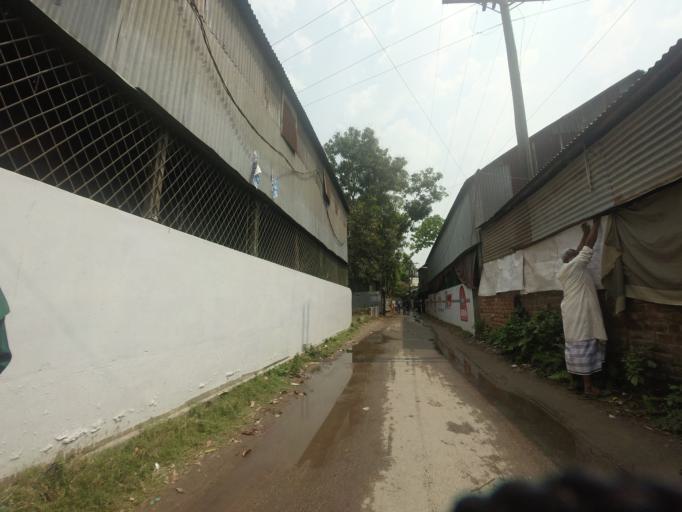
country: BD
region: Rajshahi
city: Sirajganj
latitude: 24.3271
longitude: 89.6923
